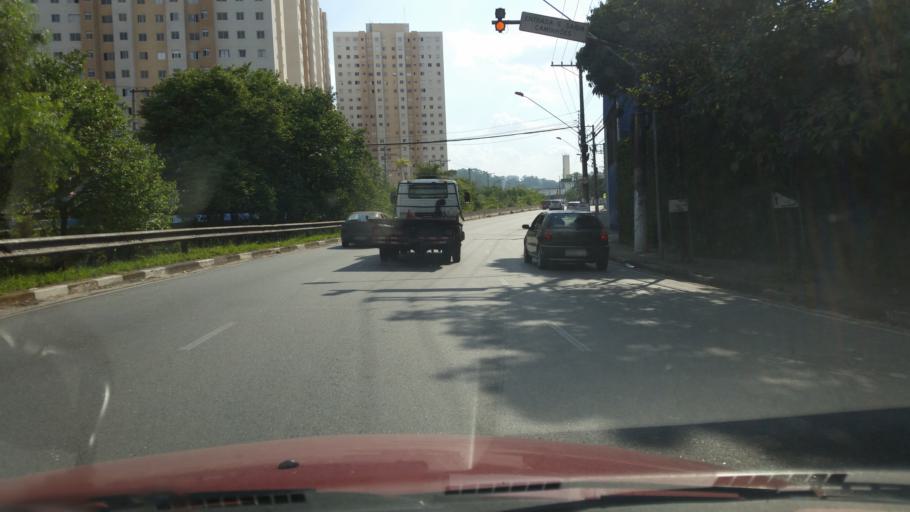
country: BR
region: Sao Paulo
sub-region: Diadema
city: Diadema
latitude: -23.6805
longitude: -46.5973
